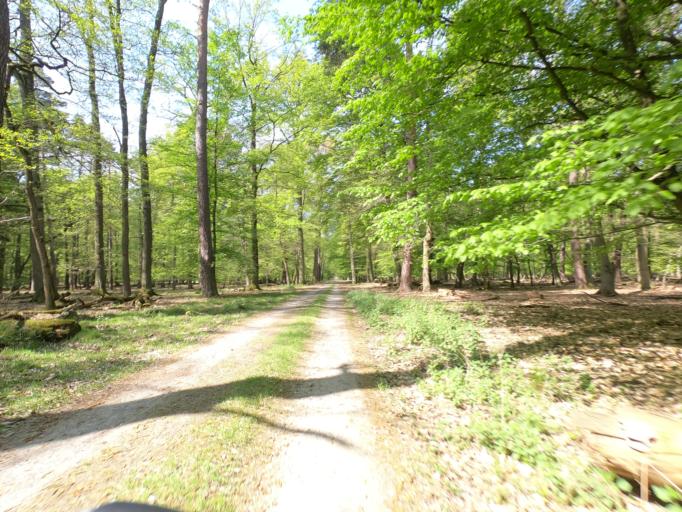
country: DE
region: Hesse
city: Kelsterbach
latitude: 50.0192
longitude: 8.5406
